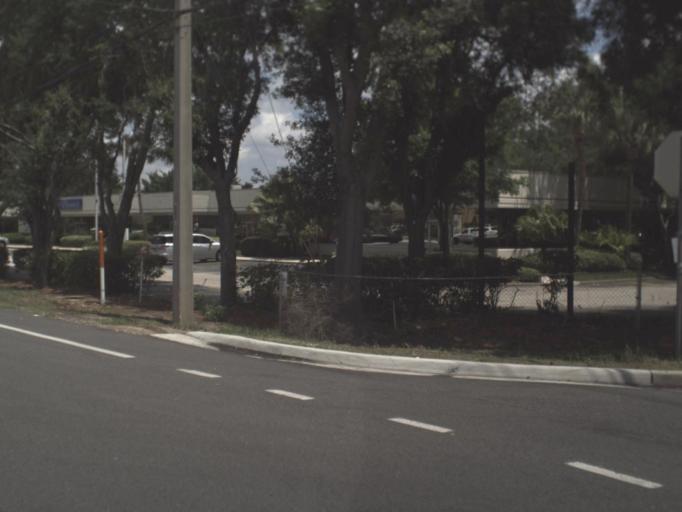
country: US
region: Florida
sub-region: Saint Johns County
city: Fruit Cove
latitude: 30.2186
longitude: -81.5844
